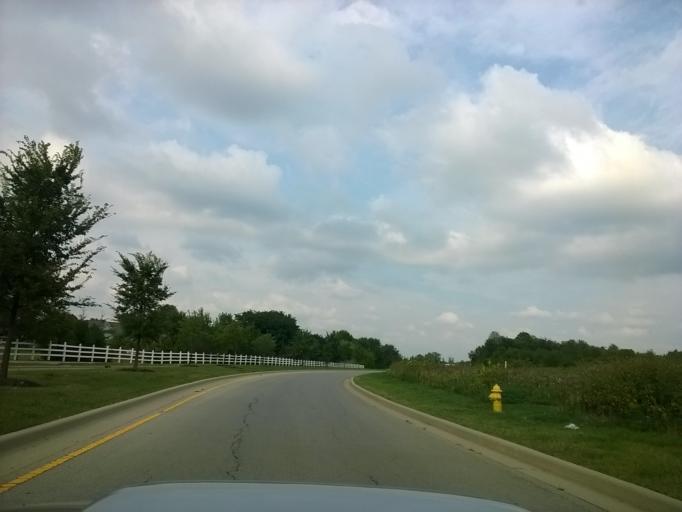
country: US
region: Indiana
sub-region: Hamilton County
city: Carmel
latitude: 39.9805
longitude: -86.1587
